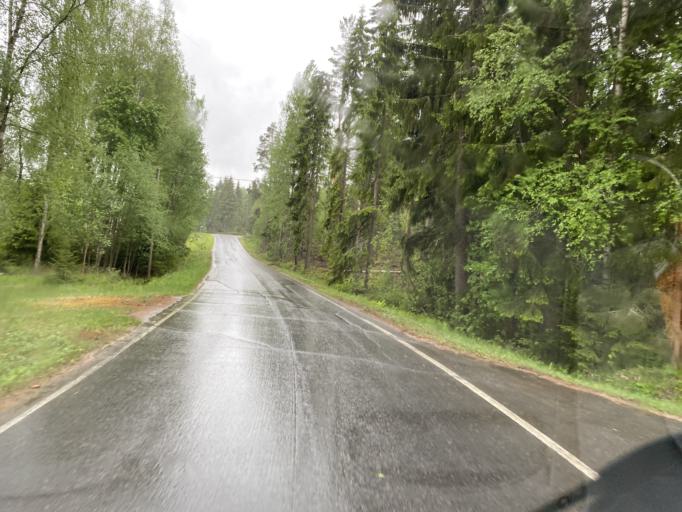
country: FI
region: Haeme
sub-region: Forssa
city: Humppila
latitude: 61.0738
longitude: 23.3114
